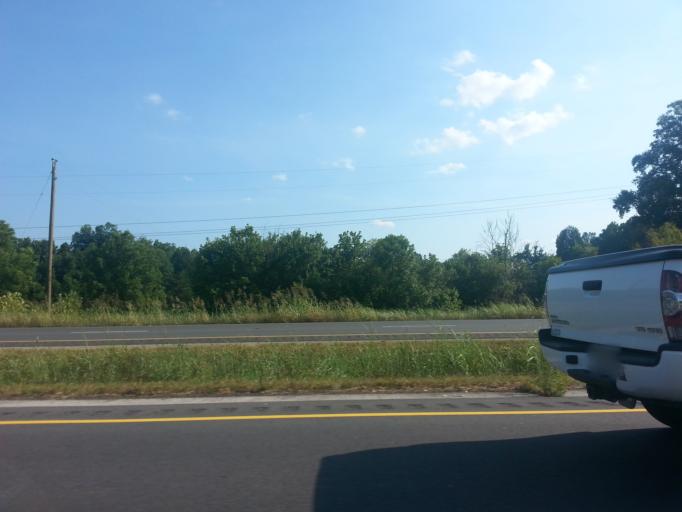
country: US
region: Tennessee
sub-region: Blount County
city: Louisville
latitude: 35.7508
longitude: -84.1180
